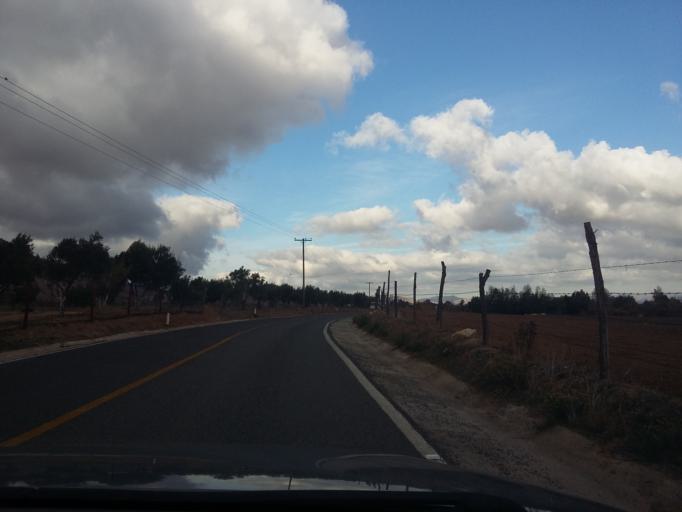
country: MX
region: Baja California
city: El Sauzal
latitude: 32.0404
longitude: -116.6708
